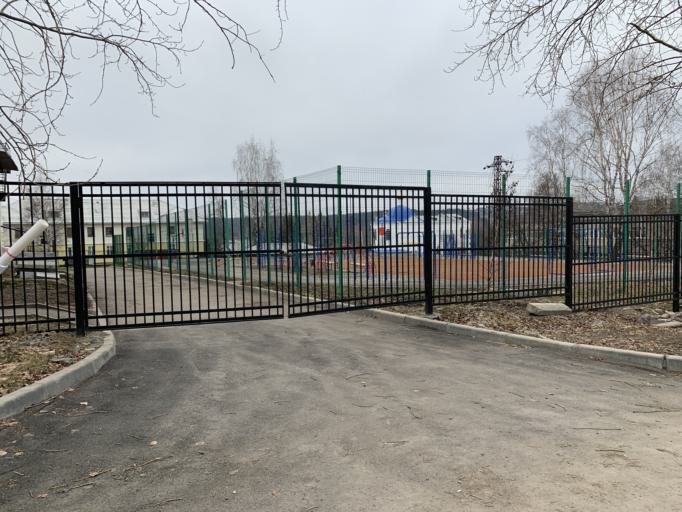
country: RU
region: Chelyabinsk
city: Nyazepetrovsk
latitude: 56.0547
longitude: 59.5976
